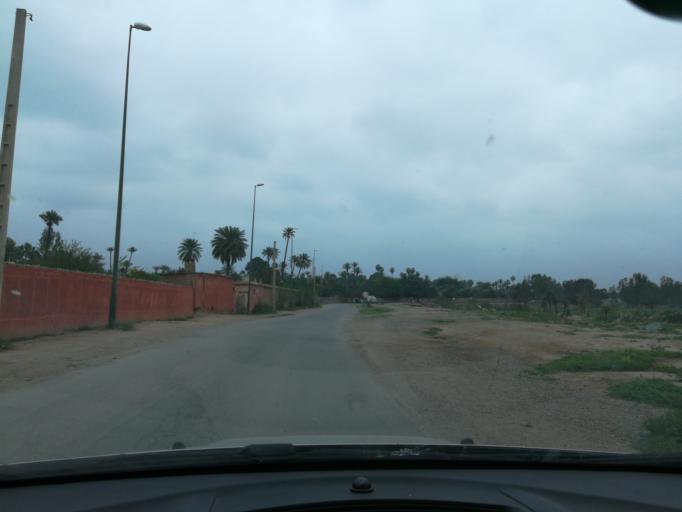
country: MA
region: Marrakech-Tensift-Al Haouz
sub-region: Marrakech
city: Marrakesh
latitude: 31.6621
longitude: -7.9836
